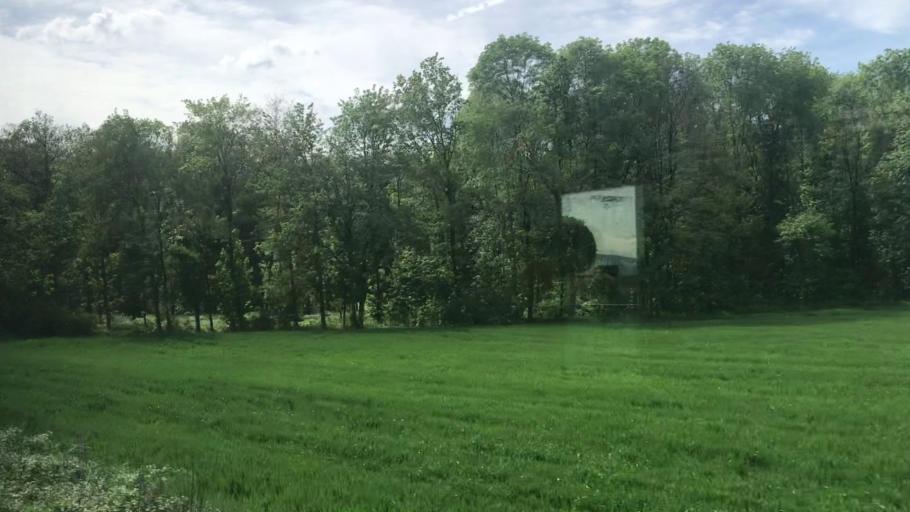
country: PL
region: Lower Silesian Voivodeship
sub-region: Powiat wroclawski
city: Katy Wroclawskie
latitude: 51.0037
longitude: 16.6931
